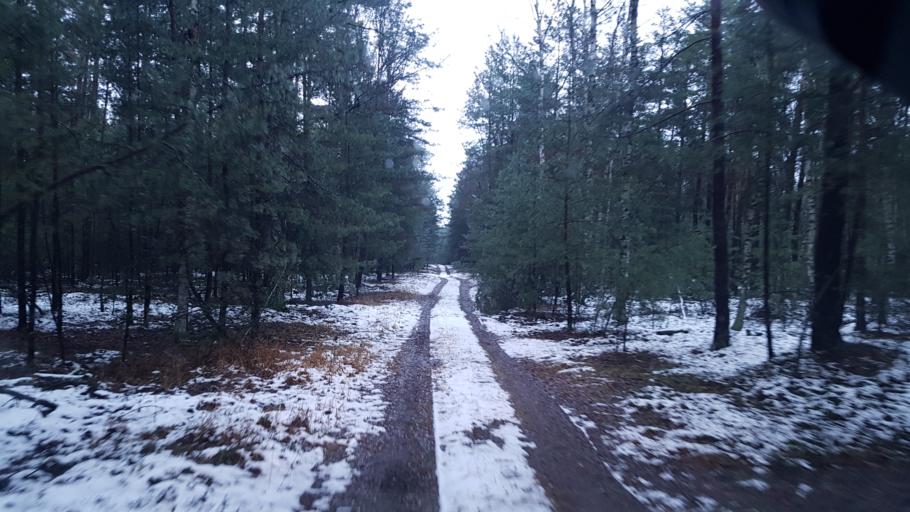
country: DE
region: Brandenburg
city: Janschwalde
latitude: 51.8858
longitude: 14.5659
